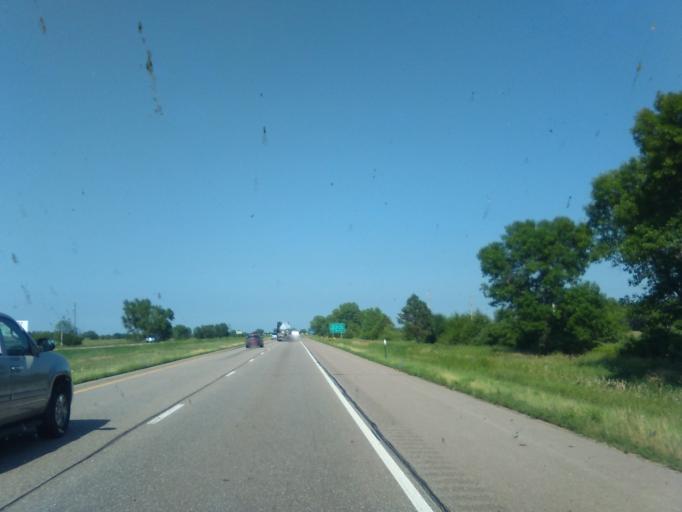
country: US
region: Nebraska
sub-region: Hall County
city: Grand Island
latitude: 40.8194
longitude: -98.4188
